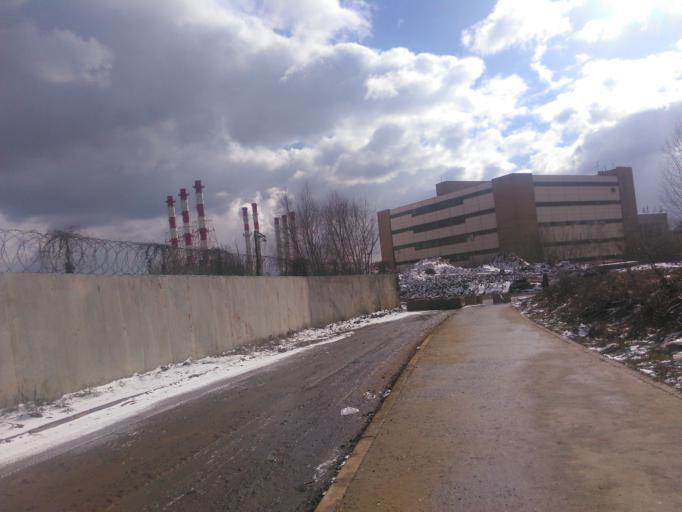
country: RU
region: Moscow
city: Nagornyy
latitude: 55.6515
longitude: 37.6393
